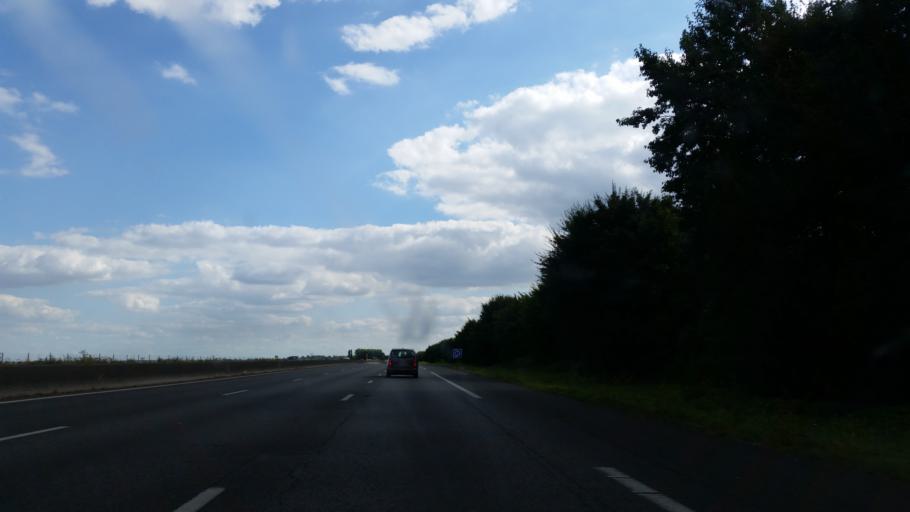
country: FR
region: Nord-Pas-de-Calais
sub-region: Departement du Pas-de-Calais
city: Vaulx-Vraucourt
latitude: 50.1591
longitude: 2.8734
